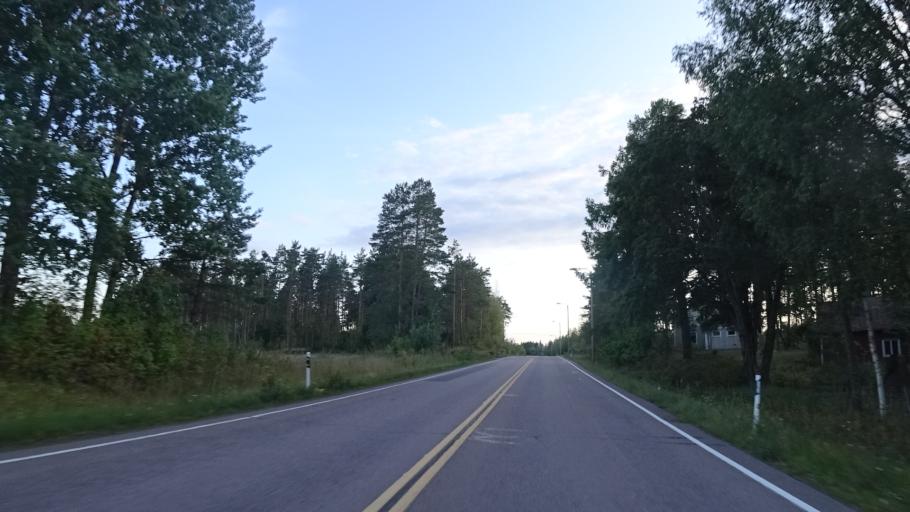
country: FI
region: South Karelia
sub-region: Lappeenranta
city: Ylaemaa
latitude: 60.6487
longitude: 27.8877
